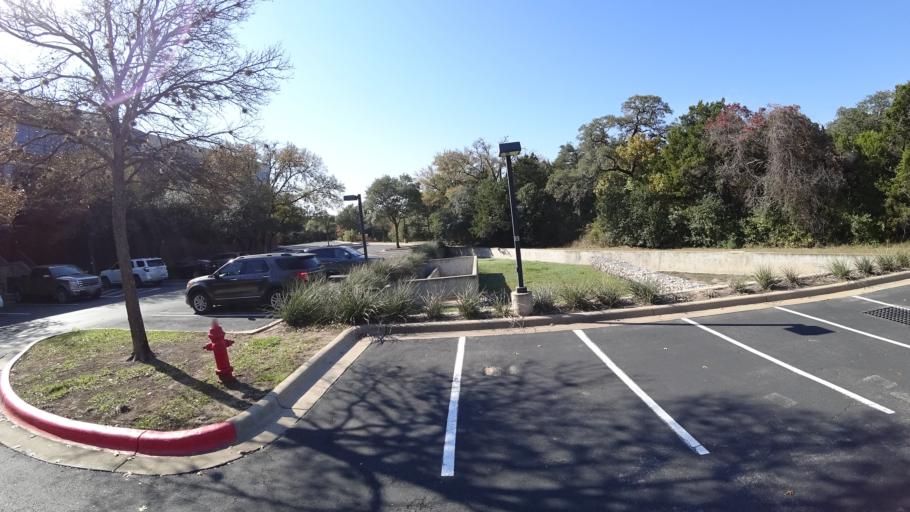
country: US
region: Texas
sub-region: Williamson County
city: Jollyville
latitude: 30.3759
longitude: -97.7833
